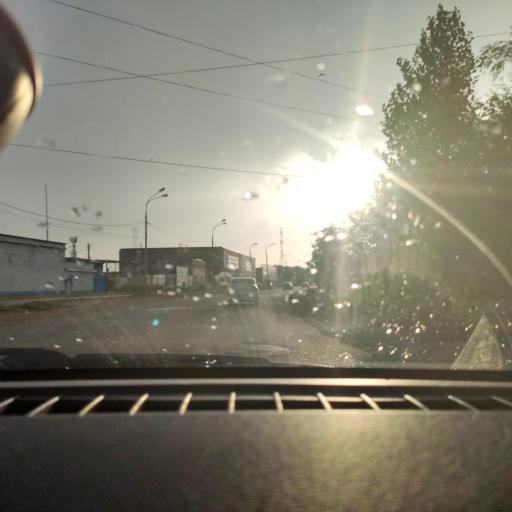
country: RU
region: Samara
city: Samara
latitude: 53.1342
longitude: 50.1211
